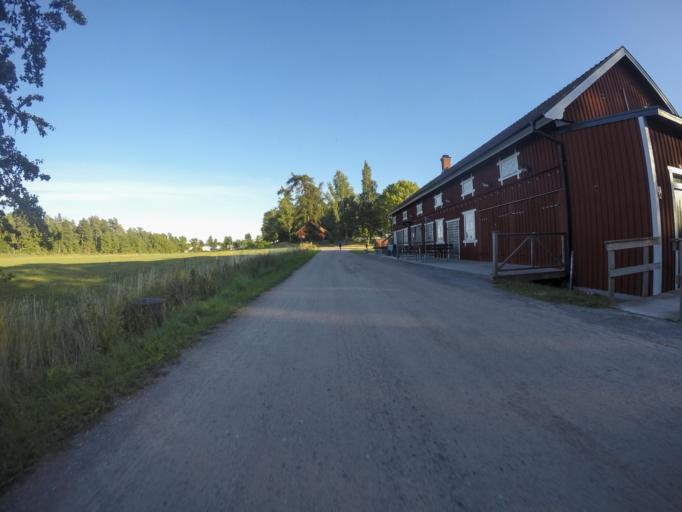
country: SE
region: Vaestmanland
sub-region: Vasteras
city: Vasteras
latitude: 59.5541
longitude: 16.6611
